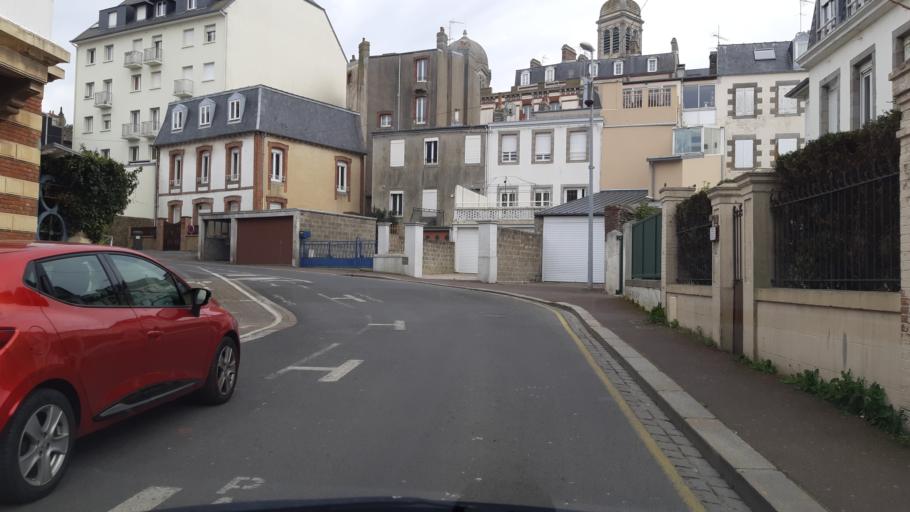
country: FR
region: Lower Normandy
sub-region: Departement de la Manche
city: Granville
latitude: 48.8379
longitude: -1.5950
